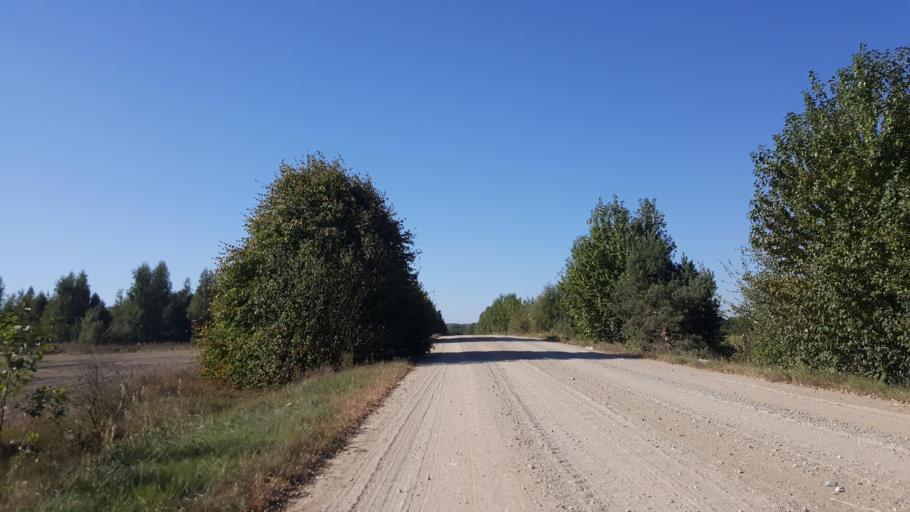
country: BY
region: Brest
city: Kamyanyets
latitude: 52.3534
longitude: 23.6921
